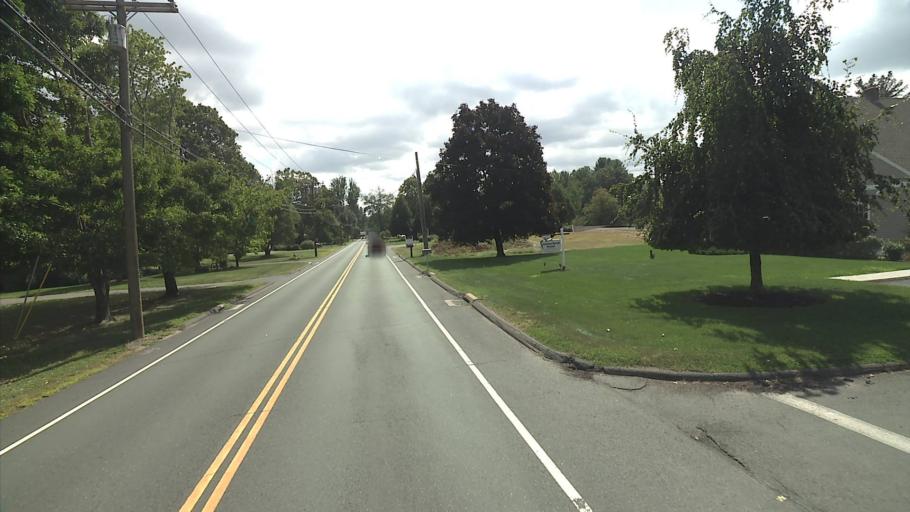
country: US
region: Connecticut
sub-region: Hartford County
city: Salmon Brook
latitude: 41.9500
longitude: -72.7845
